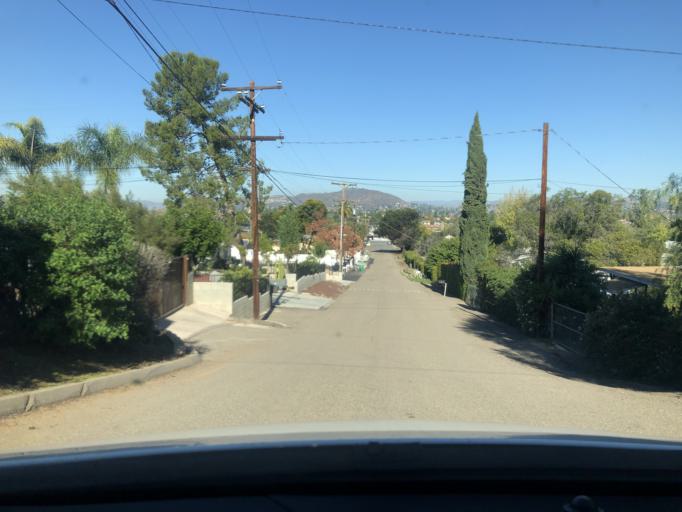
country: US
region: California
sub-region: San Diego County
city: Bostonia
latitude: 32.7849
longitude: -116.9395
